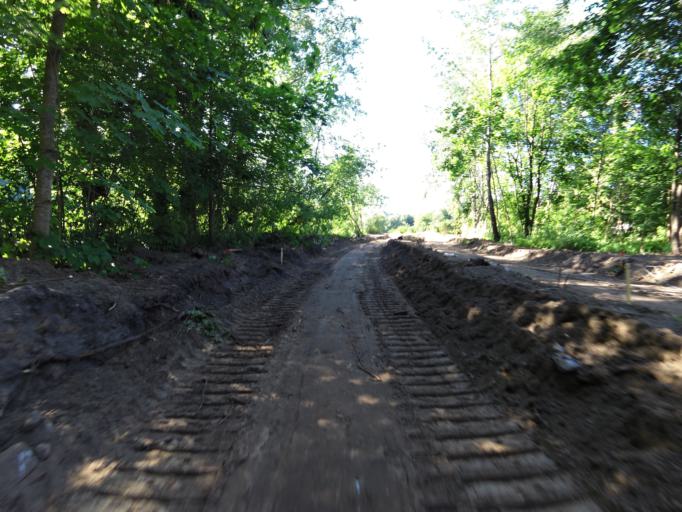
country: LT
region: Vilnius County
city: Vilkpede
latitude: 54.6857
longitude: 25.2498
